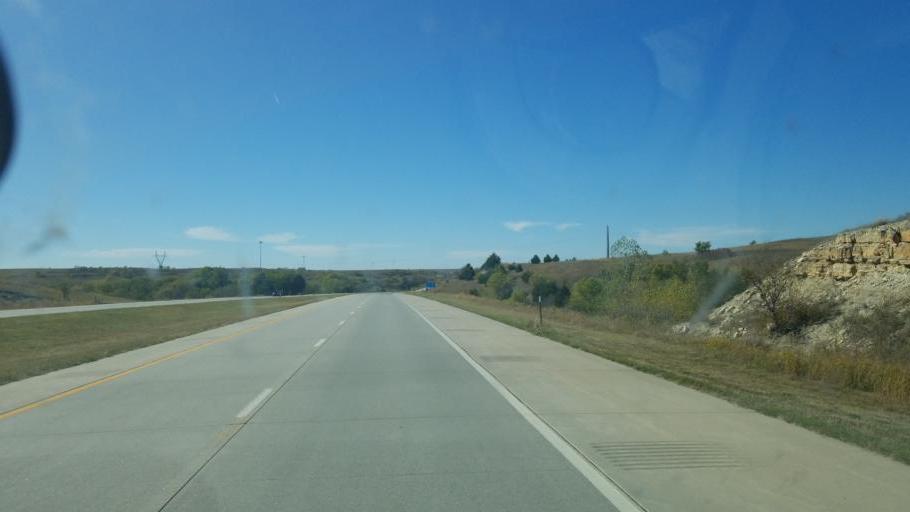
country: US
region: Kansas
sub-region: Riley County
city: Ogden
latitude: 39.0658
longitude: -96.6089
